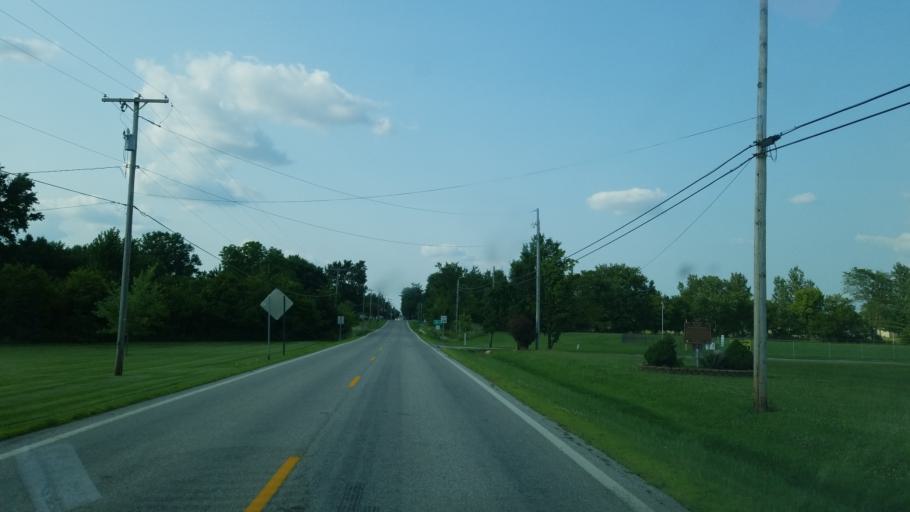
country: US
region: Ohio
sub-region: Union County
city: Richwood
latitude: 40.3478
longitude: -83.2640
